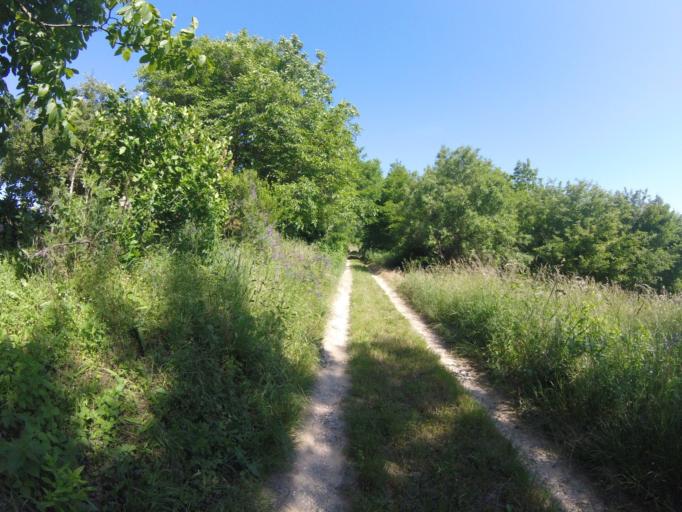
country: HU
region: Zala
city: Zalaszentgrot
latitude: 46.8979
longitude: 17.0677
